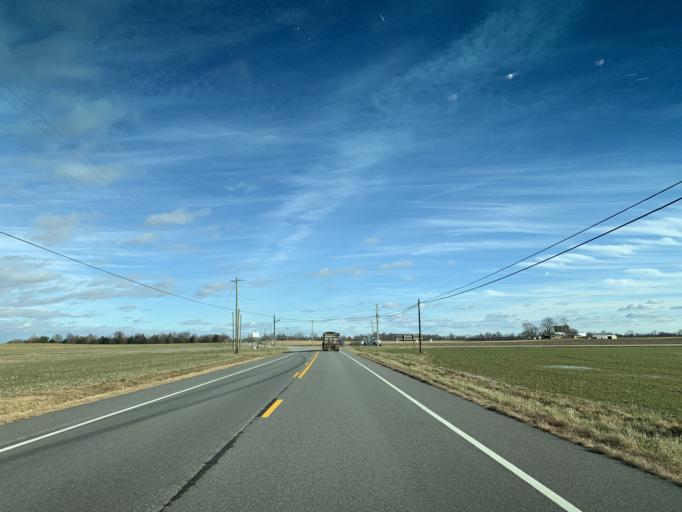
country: US
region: Maryland
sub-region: Queen Anne's County
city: Kingstown
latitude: 39.3237
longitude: -76.0256
